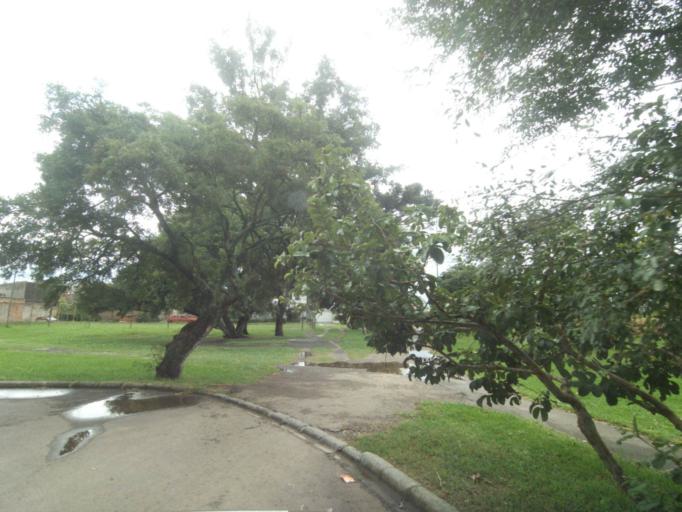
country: BR
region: Parana
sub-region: Pinhais
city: Pinhais
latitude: -25.4662
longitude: -49.1906
